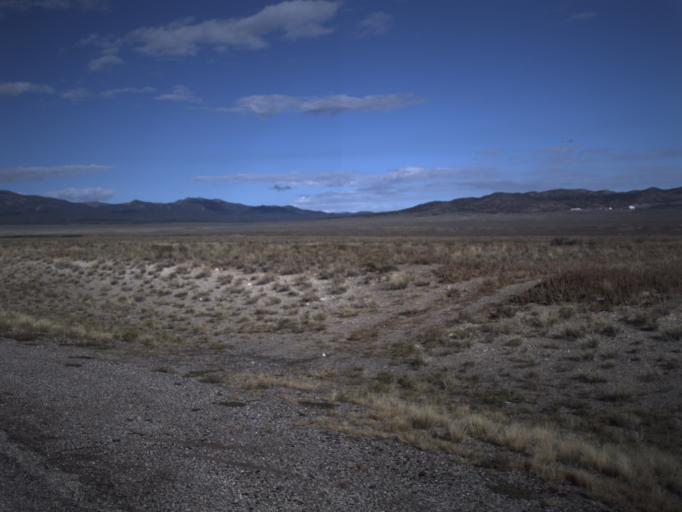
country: US
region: Utah
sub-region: Beaver County
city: Milford
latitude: 38.4246
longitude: -113.1147
